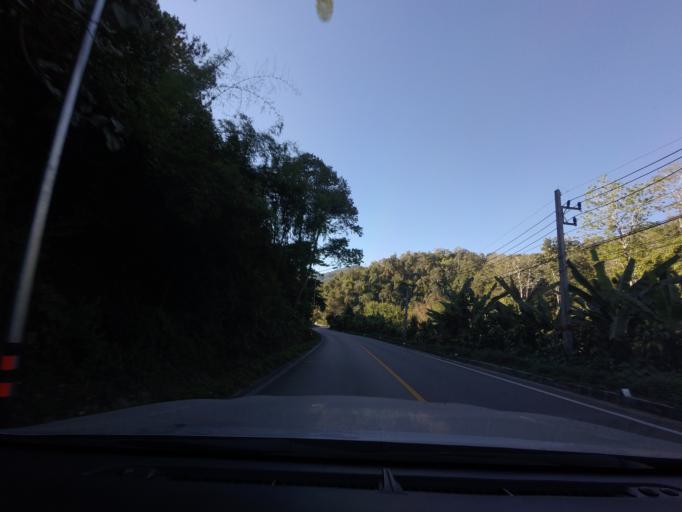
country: TH
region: Mae Hong Son
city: Mae Hi
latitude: 19.2043
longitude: 98.6781
